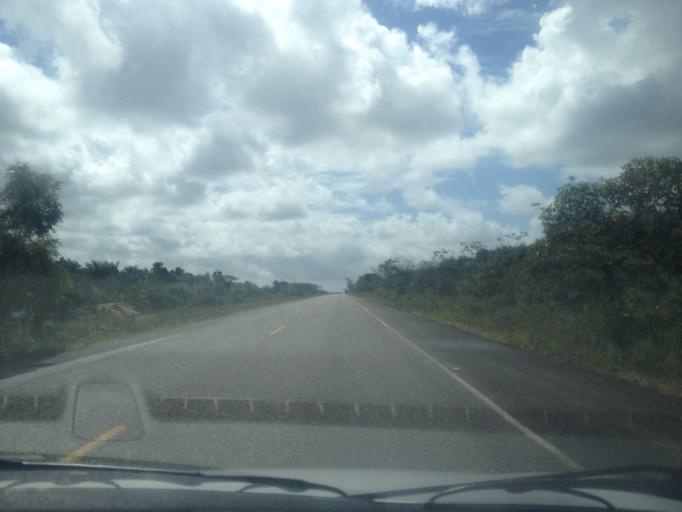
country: BR
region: Bahia
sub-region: Entre Rios
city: Entre Rios
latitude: -12.2564
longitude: -37.8660
